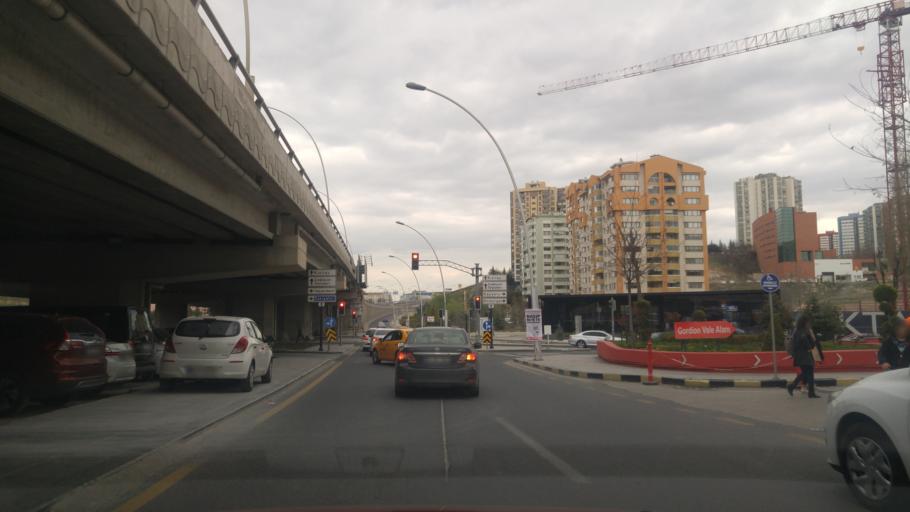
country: TR
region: Ankara
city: Batikent
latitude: 39.9020
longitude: 32.6912
